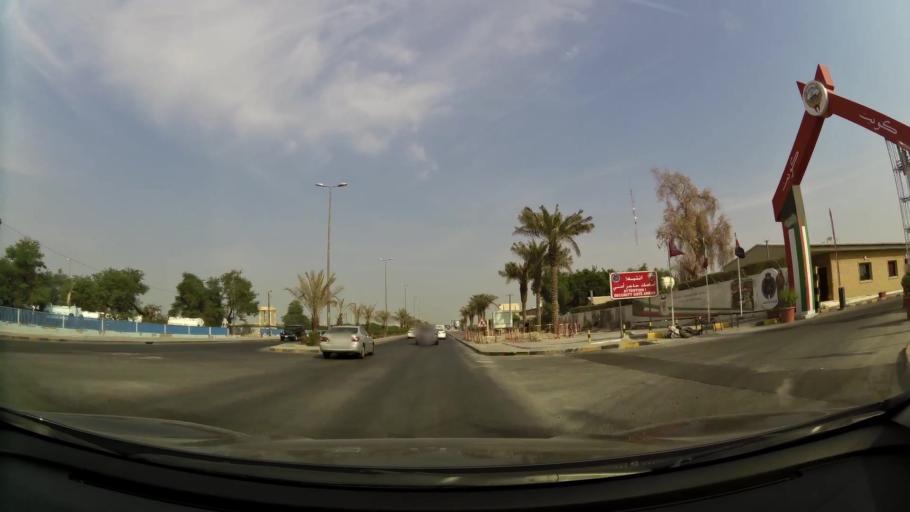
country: KW
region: Al Asimah
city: Ar Rabiyah
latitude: 29.3076
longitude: 47.9513
